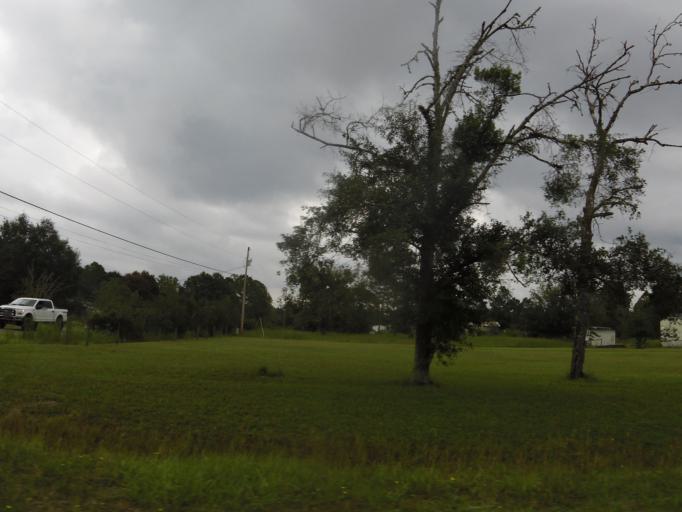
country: US
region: Florida
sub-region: Clay County
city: Middleburg
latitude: 30.1269
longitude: -81.9493
